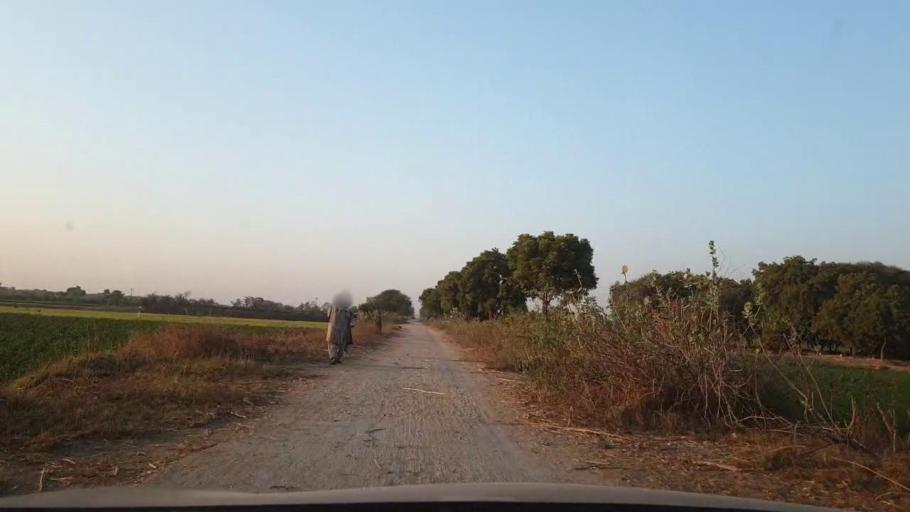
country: PK
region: Sindh
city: Tando Allahyar
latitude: 25.5098
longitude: 68.7408
